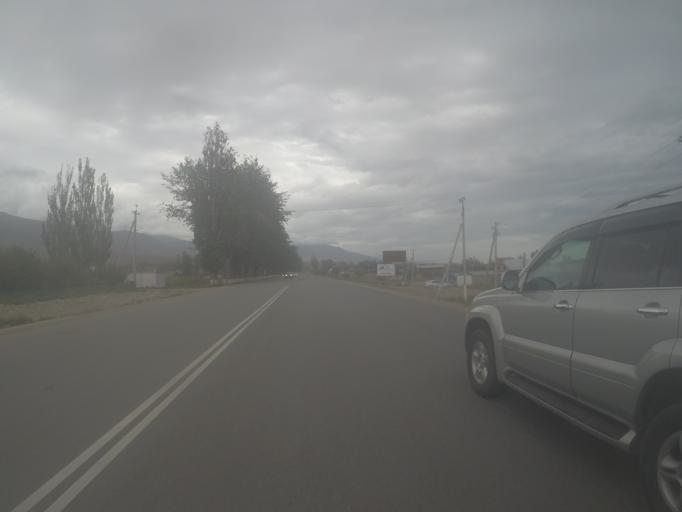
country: KG
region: Ysyk-Koel
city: Cholpon-Ata
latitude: 42.5895
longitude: 76.7496
